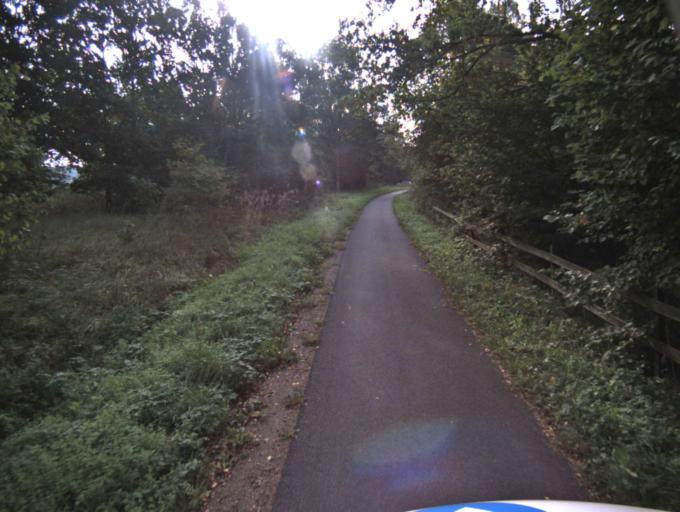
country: SE
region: Vaestra Goetaland
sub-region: Ulricehamns Kommun
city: Ulricehamn
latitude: 57.7424
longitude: 13.3973
